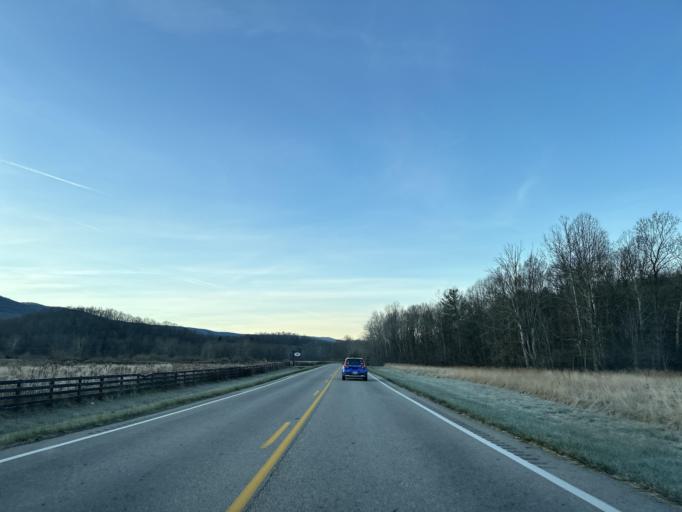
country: US
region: Virginia
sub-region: Augusta County
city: Jolivue
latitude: 38.1181
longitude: -79.2921
